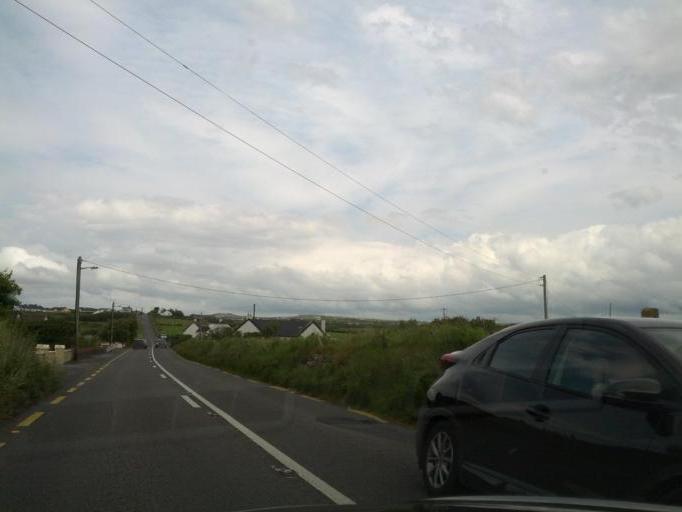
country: IE
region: Munster
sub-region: An Clar
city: Kilrush
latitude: 52.8422
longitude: -9.4254
